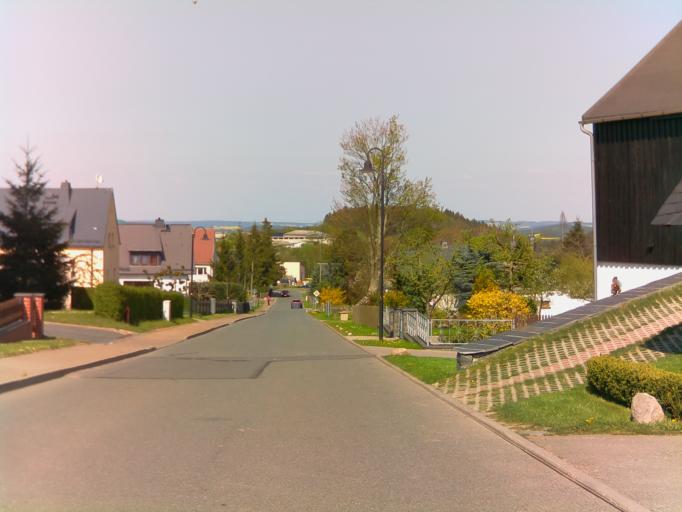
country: DE
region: Saxony
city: Mehltheuer
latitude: 50.5667
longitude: 12.0413
